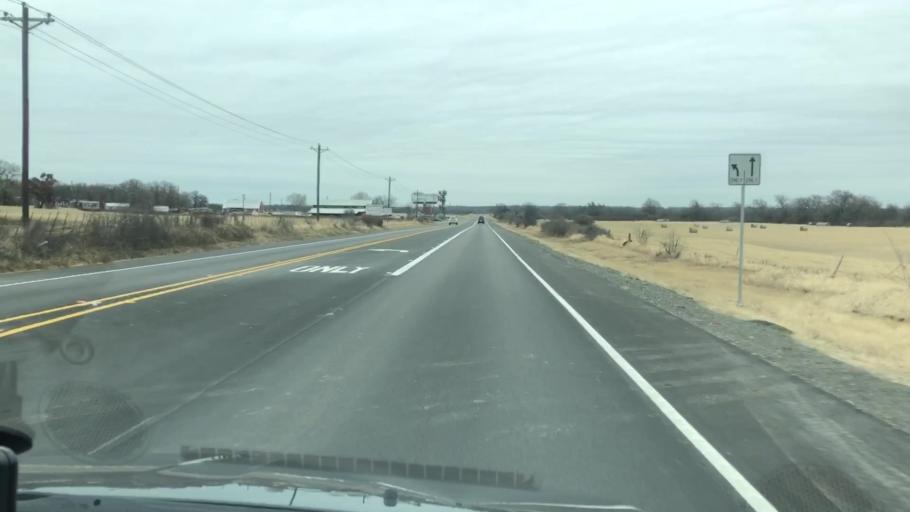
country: US
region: Texas
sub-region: Palo Pinto County
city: Mineral Wells
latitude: 32.5350
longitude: -98.1233
